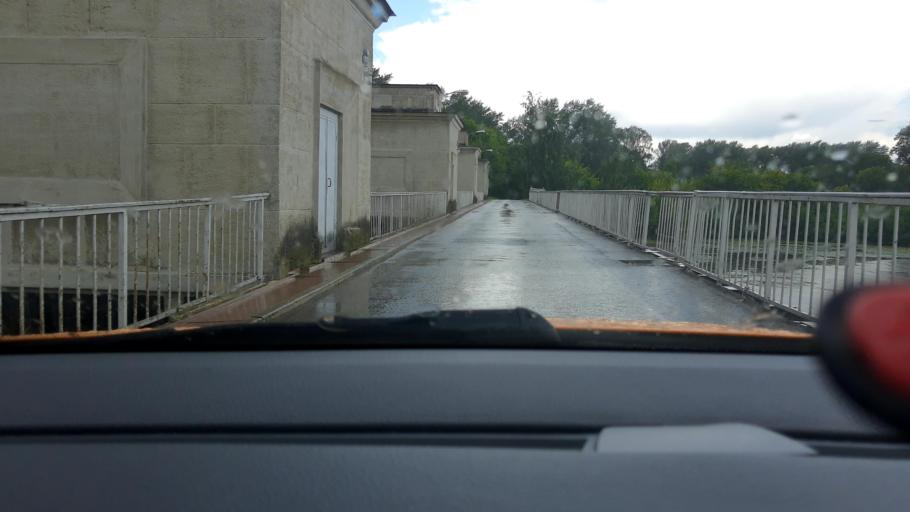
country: RU
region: Moscow
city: Mar'ino
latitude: 55.6724
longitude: 37.7143
